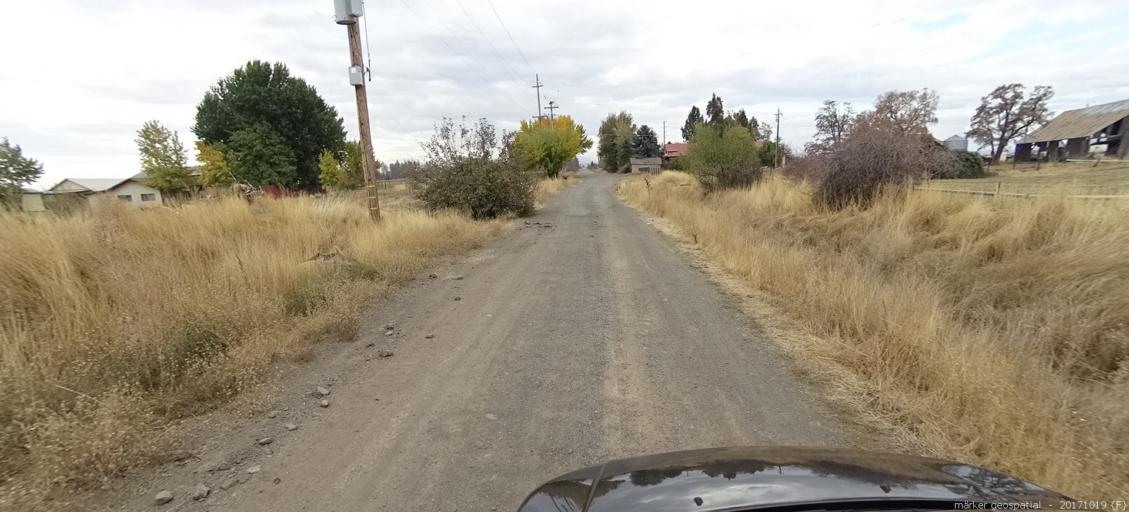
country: US
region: California
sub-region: Shasta County
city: Burney
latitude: 41.0670
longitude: -121.3891
